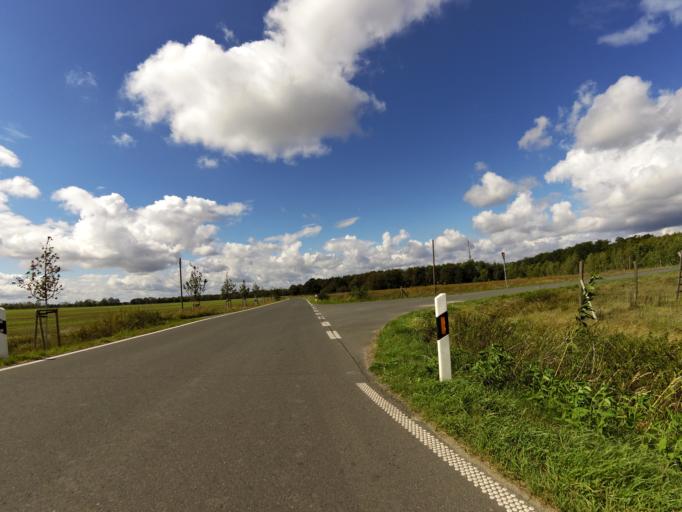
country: DE
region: Brandenburg
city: Grossbeeren
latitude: 52.3720
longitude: 13.3476
